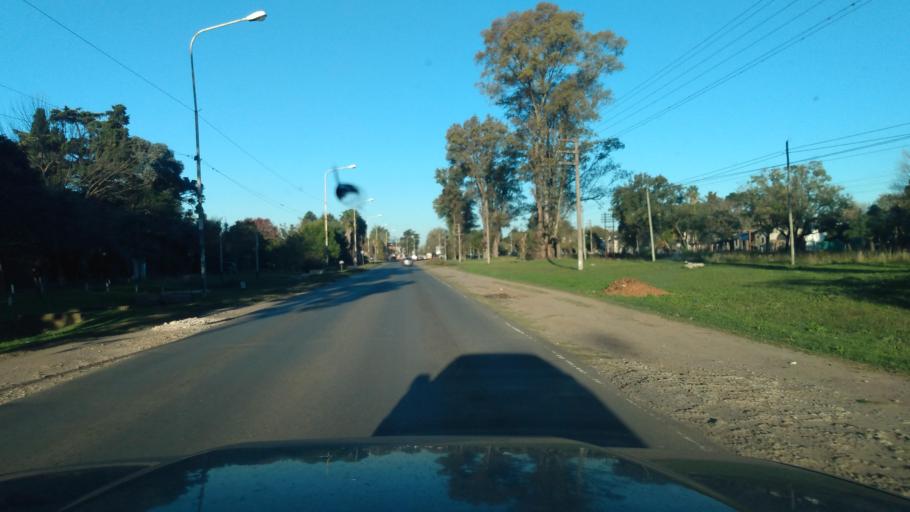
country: AR
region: Buenos Aires
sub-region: Partido de Merlo
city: Merlo
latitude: -34.6382
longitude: -58.8324
